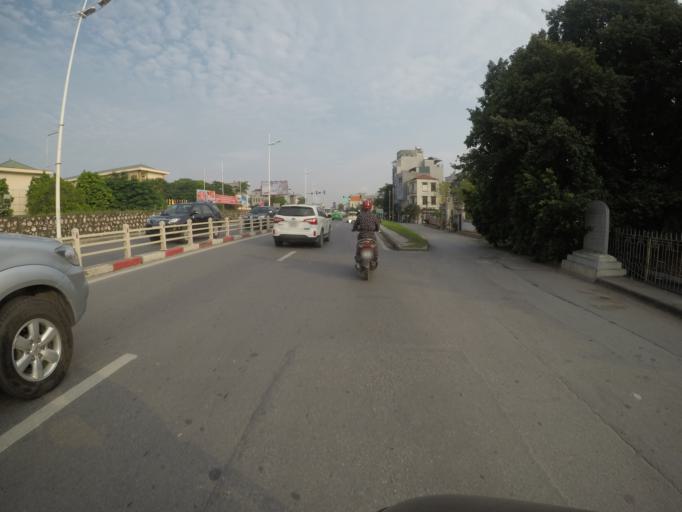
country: VN
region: Ha Noi
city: Tay Ho
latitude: 21.0762
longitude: 105.8217
